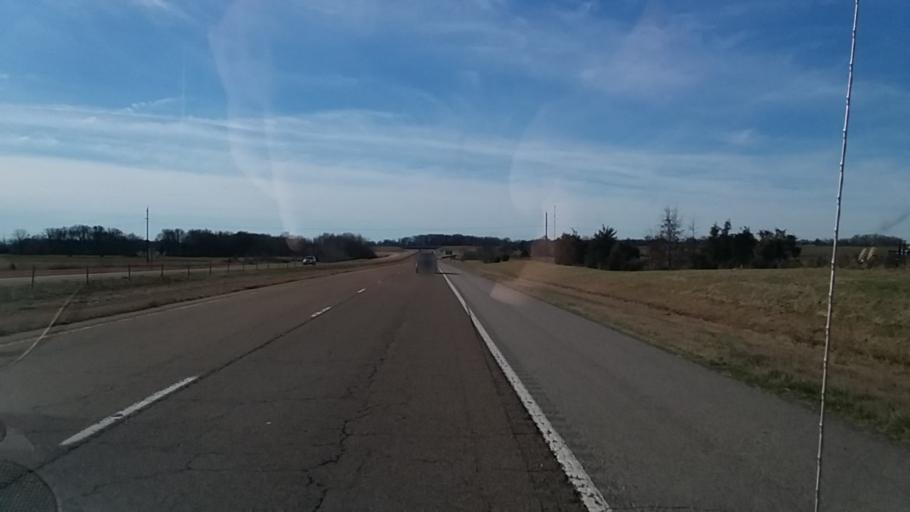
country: US
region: Tennessee
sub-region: Crockett County
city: Alamo
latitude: 35.8083
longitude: -89.1606
